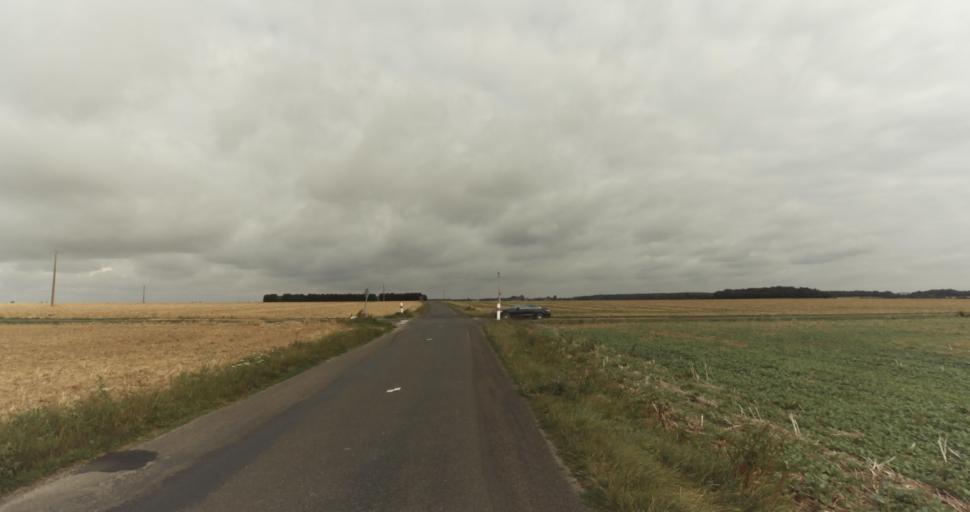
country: FR
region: Haute-Normandie
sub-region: Departement de l'Eure
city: La Couture-Boussey
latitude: 48.9177
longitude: 1.4045
